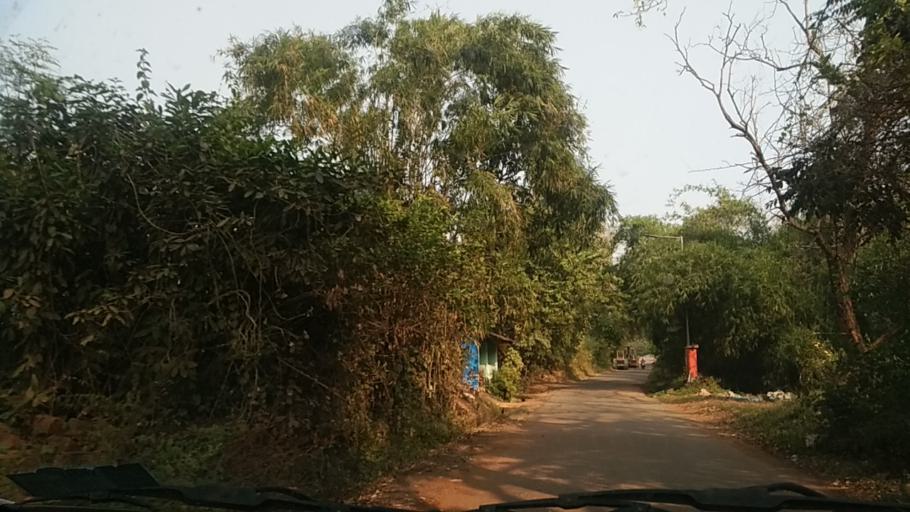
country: IN
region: Goa
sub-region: South Goa
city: Raia
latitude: 15.3165
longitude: 73.9466
